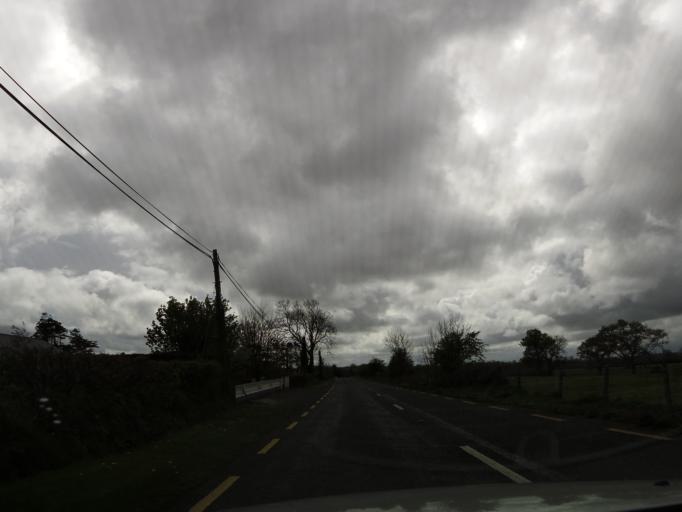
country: IE
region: Connaught
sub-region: Maigh Eo
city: Claremorris
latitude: 53.6957
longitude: -9.0163
